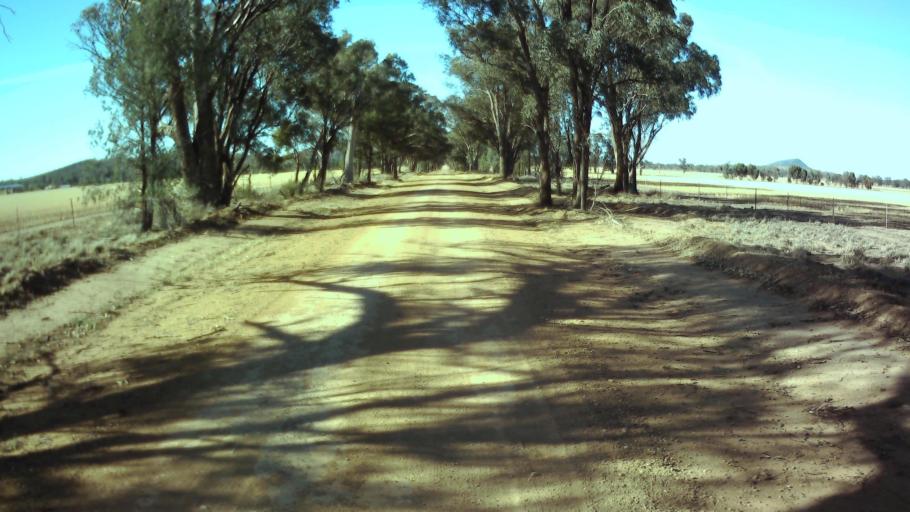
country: AU
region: New South Wales
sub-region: Weddin
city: Grenfell
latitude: -33.8147
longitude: 147.8766
